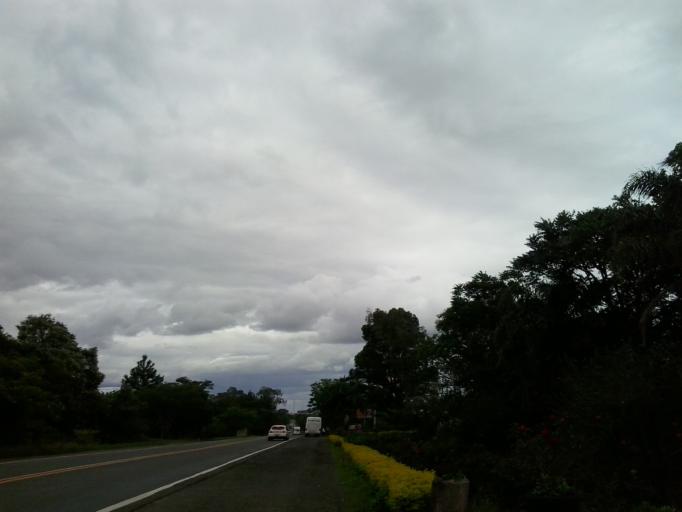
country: BR
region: Rio Grande do Sul
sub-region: Santa Maria
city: Santa Maria
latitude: -29.7325
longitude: -53.5394
